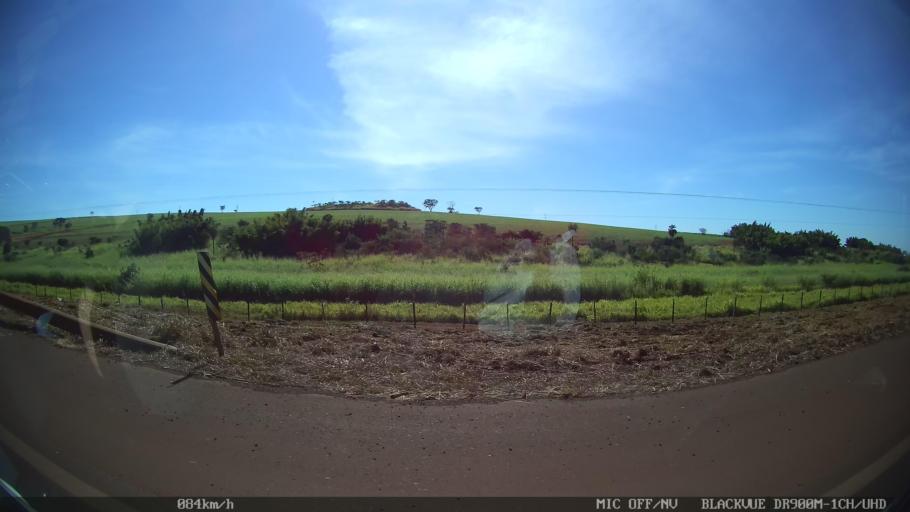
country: BR
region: Sao Paulo
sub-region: Ipua
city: Ipua
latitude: -20.4926
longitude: -48.0091
